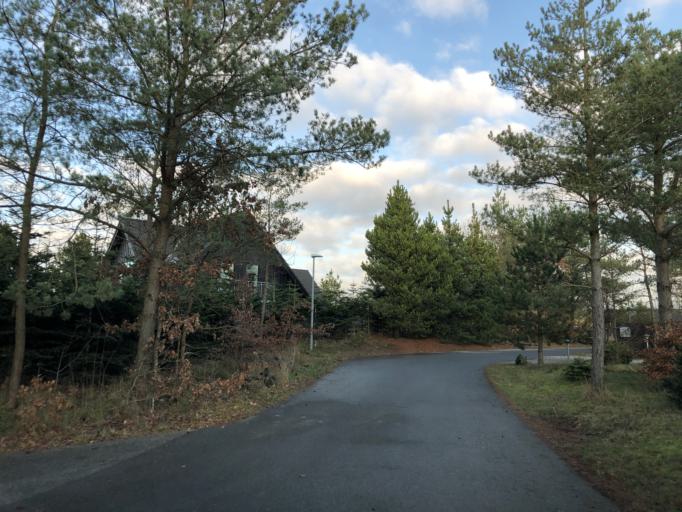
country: DK
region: Central Jutland
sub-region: Holstebro Kommune
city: Ulfborg
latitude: 56.3193
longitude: 8.4370
